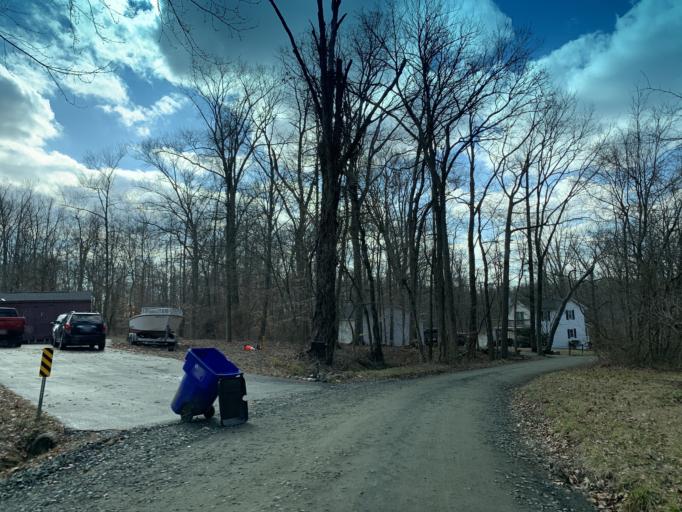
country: US
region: Maryland
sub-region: Harford County
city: Riverside
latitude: 39.5044
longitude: -76.2509
